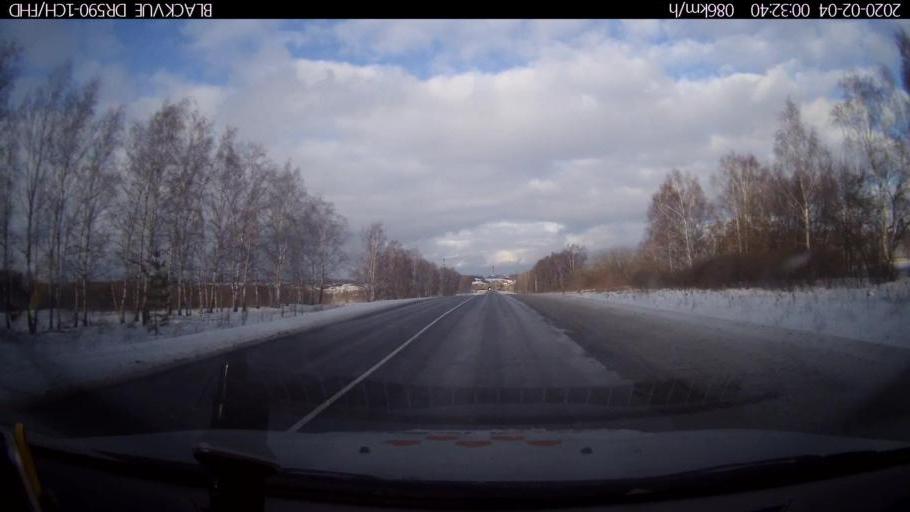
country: RU
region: Nizjnij Novgorod
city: Kstovo
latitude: 56.0618
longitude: 44.1396
